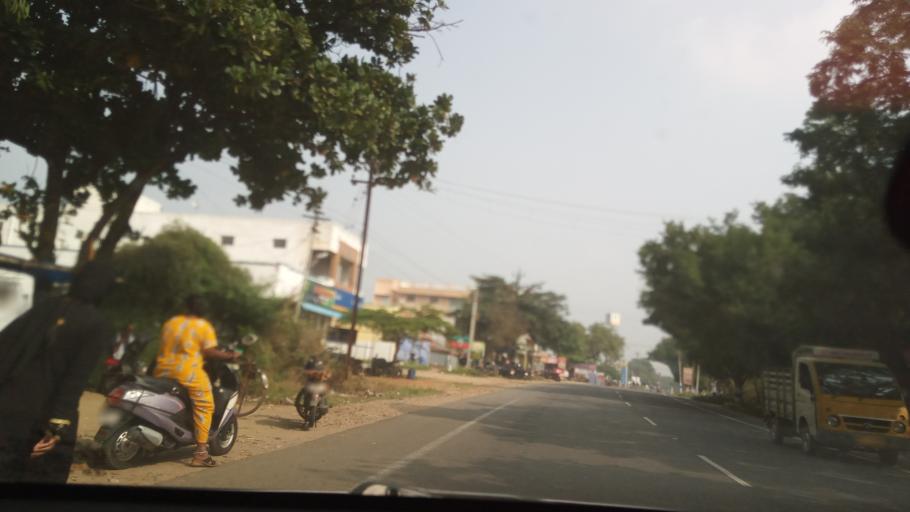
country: IN
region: Tamil Nadu
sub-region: Erode
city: Punjai Puliyampatti
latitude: 11.3607
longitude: 77.1699
